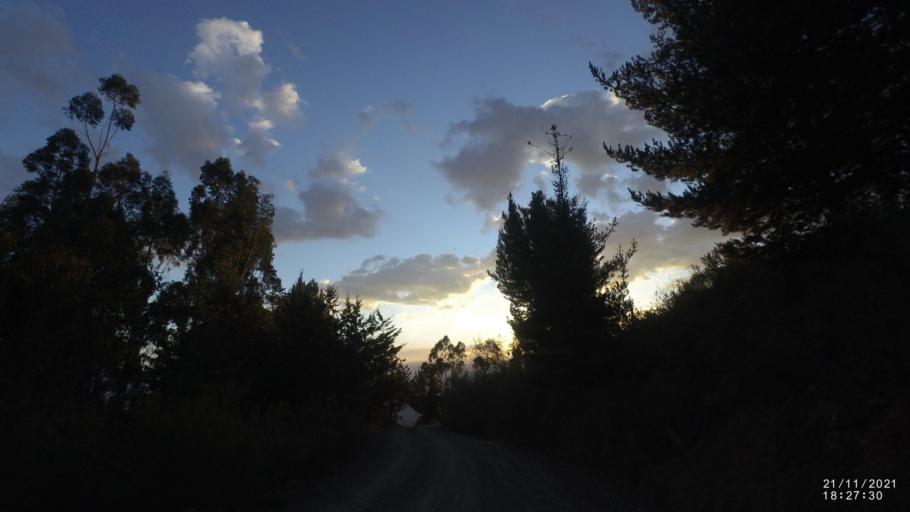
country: BO
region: Cochabamba
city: Cochabamba
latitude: -17.3063
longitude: -66.2179
